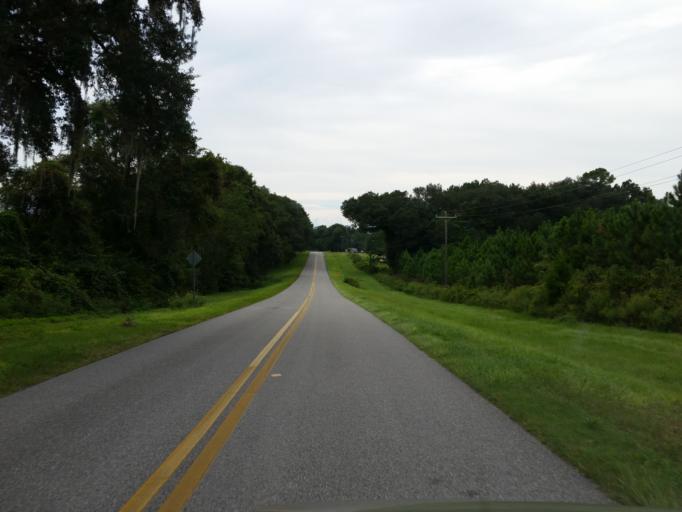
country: US
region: Florida
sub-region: Alachua County
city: High Springs
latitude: 29.9513
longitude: -82.5098
